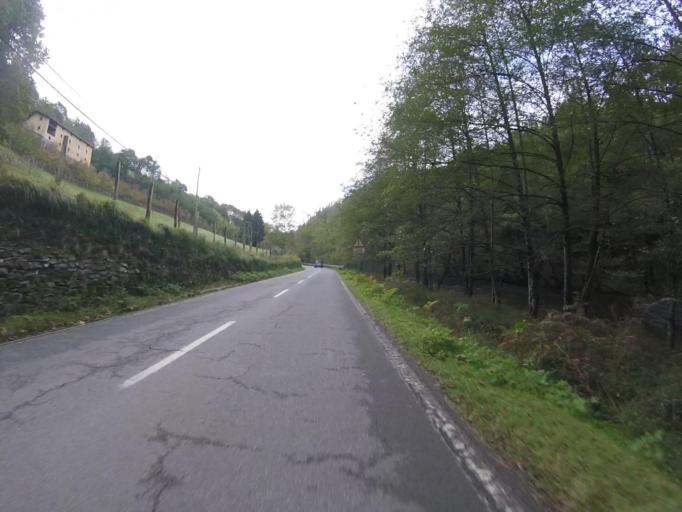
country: ES
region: Navarre
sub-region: Provincia de Navarra
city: Goizueta
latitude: 43.1856
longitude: -1.8581
